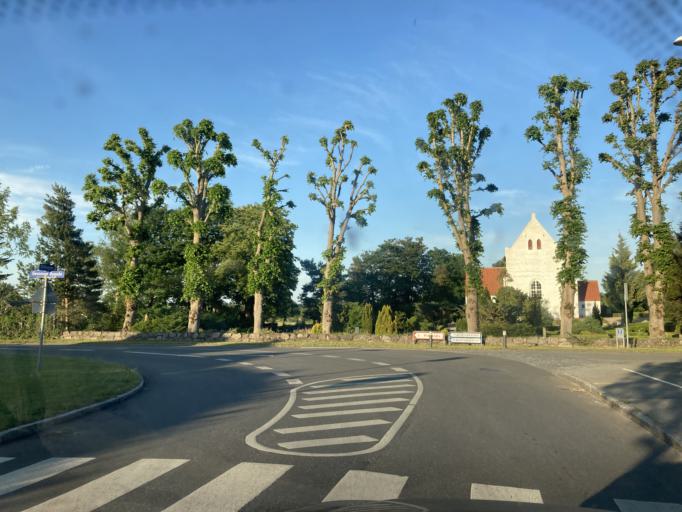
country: DK
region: Zealand
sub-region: Lejre Kommune
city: Lejre
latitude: 55.6485
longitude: 11.9616
